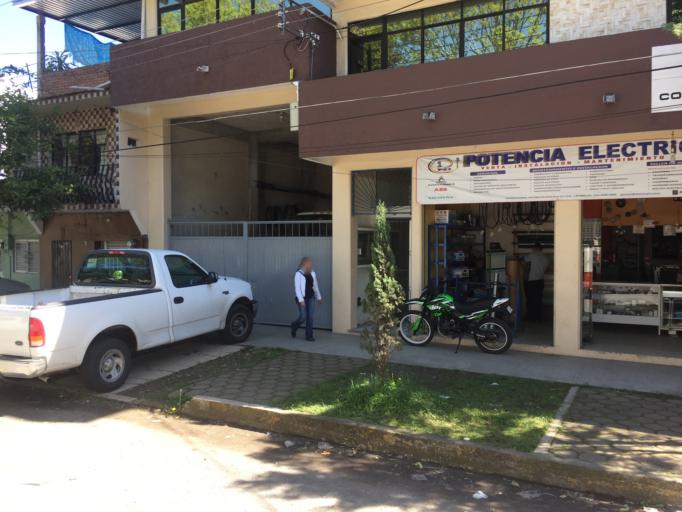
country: MX
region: Veracruz
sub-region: Xalapa
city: Xalapa de Enriquez
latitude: 19.5346
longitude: -96.9120
